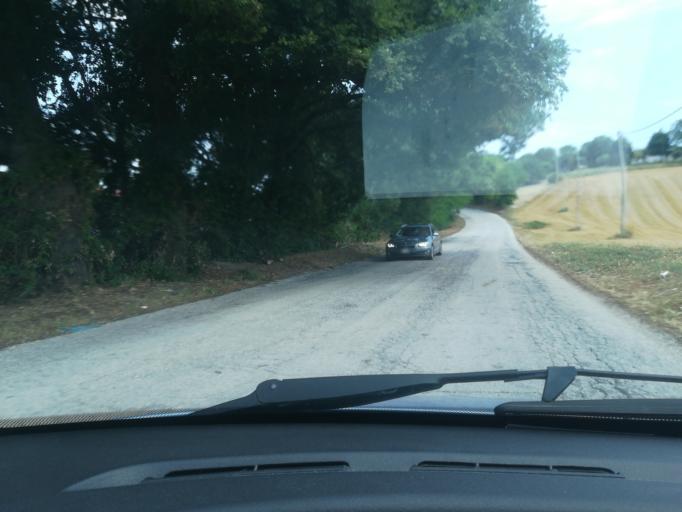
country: IT
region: The Marches
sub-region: Provincia di Macerata
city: Sforzacosta
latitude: 43.2628
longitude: 13.4394
